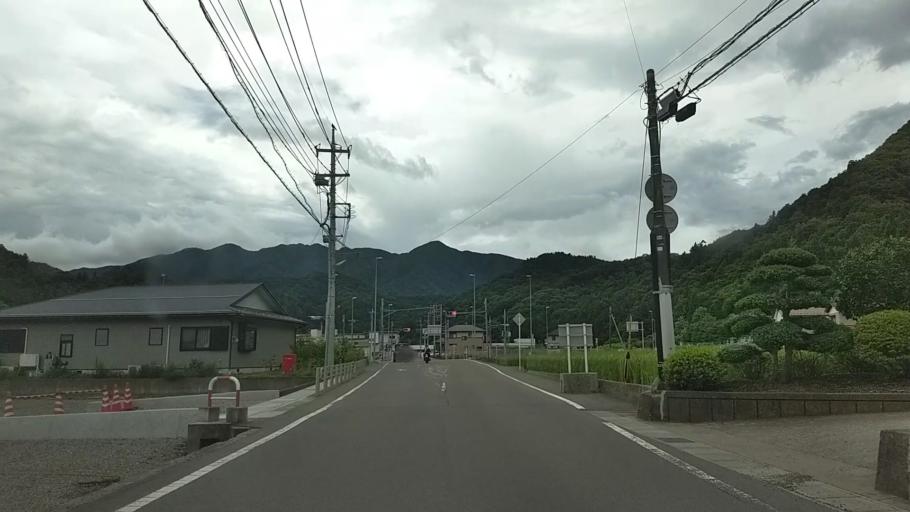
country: JP
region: Yamanashi
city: Otsuki
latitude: 35.5715
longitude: 138.9312
